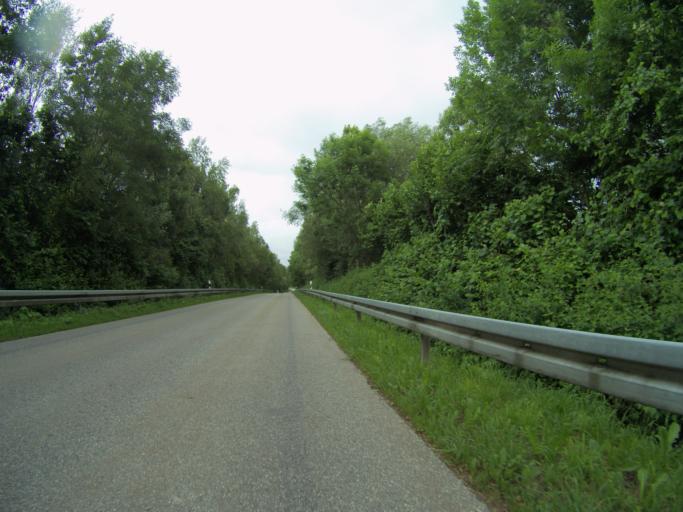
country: DE
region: Bavaria
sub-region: Upper Bavaria
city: Marzling
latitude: 48.3912
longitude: 11.7980
